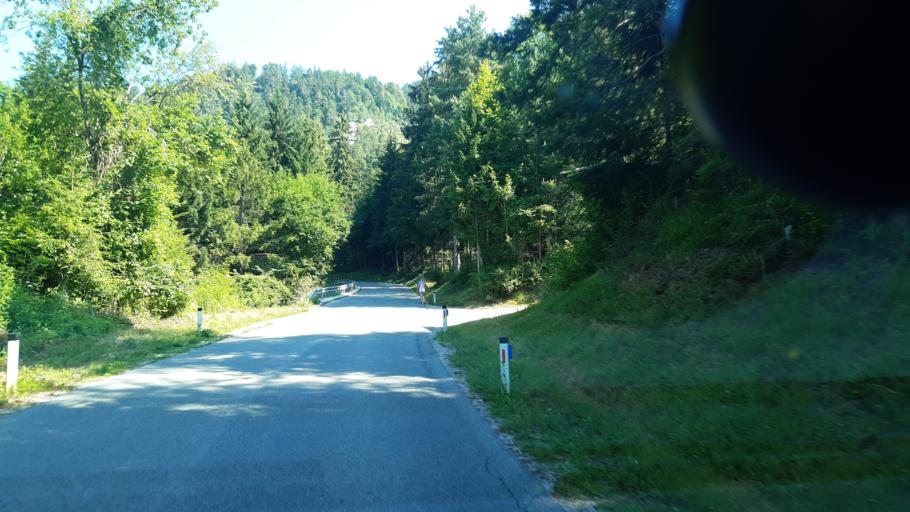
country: SI
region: Trzic
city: Bistrica pri Trzicu
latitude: 46.3599
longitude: 14.2866
